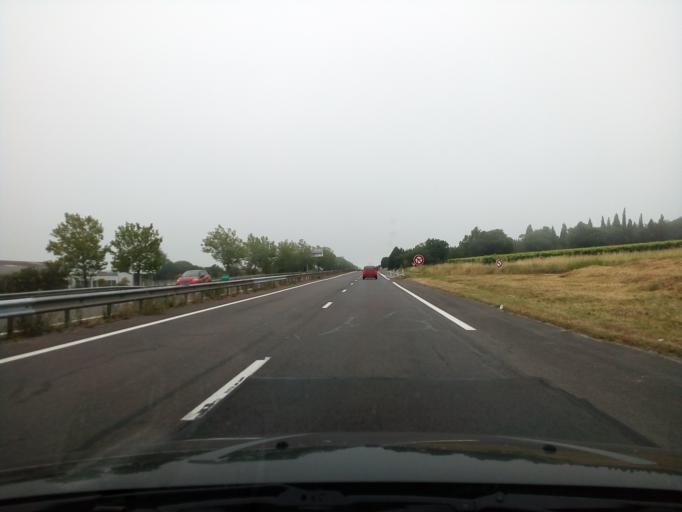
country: FR
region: Poitou-Charentes
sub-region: Departement de la Charente
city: Saint-Brice
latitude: 45.6768
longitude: -0.2758
